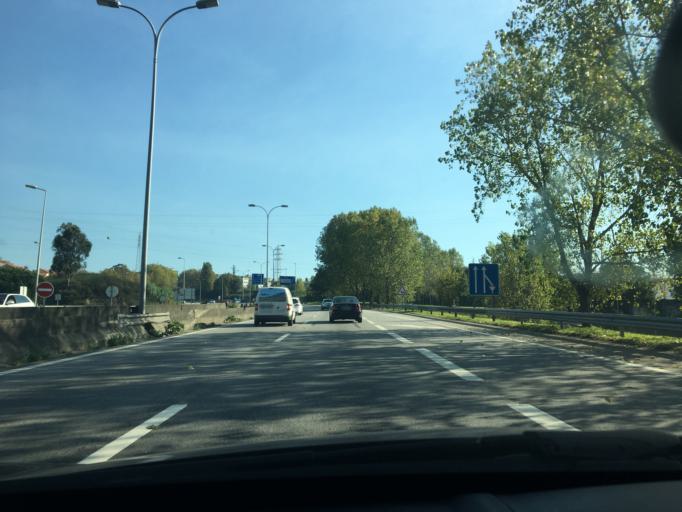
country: PT
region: Porto
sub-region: Matosinhos
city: Matosinhos
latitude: 41.1916
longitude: -8.6793
